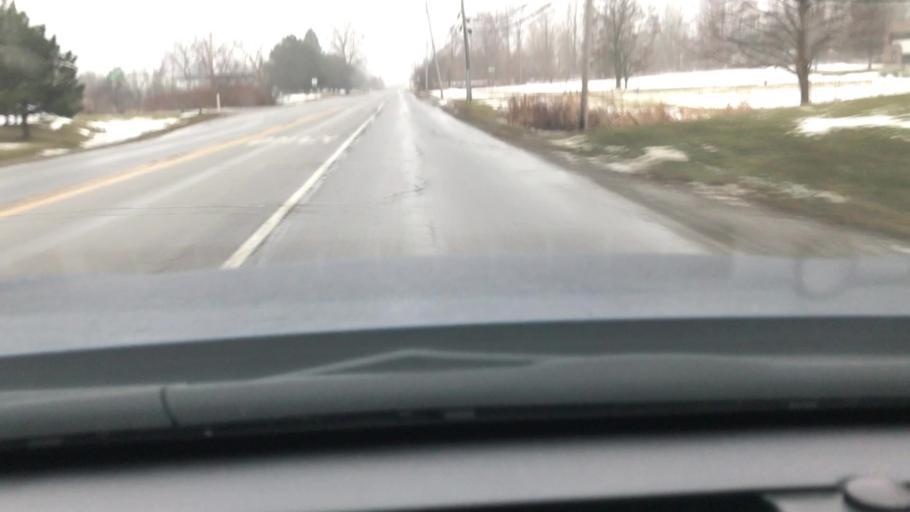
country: US
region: Michigan
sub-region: Oakland County
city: Wixom
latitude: 42.5050
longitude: -83.5163
